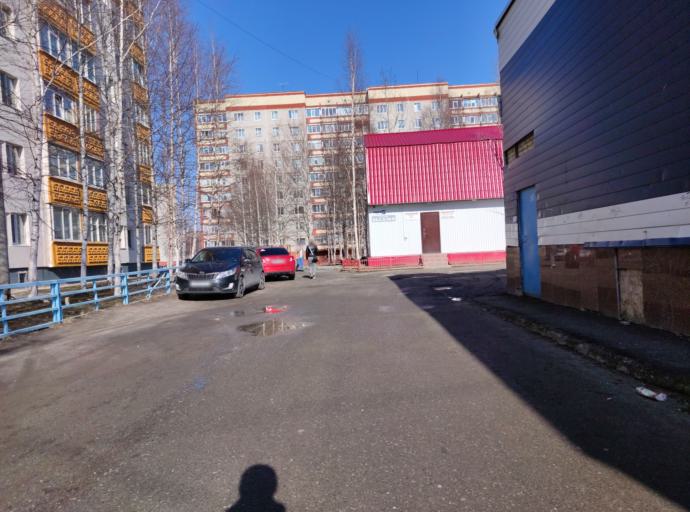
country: RU
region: Khanty-Mansiyskiy Avtonomnyy Okrug
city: Langepas
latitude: 61.2494
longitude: 75.1788
